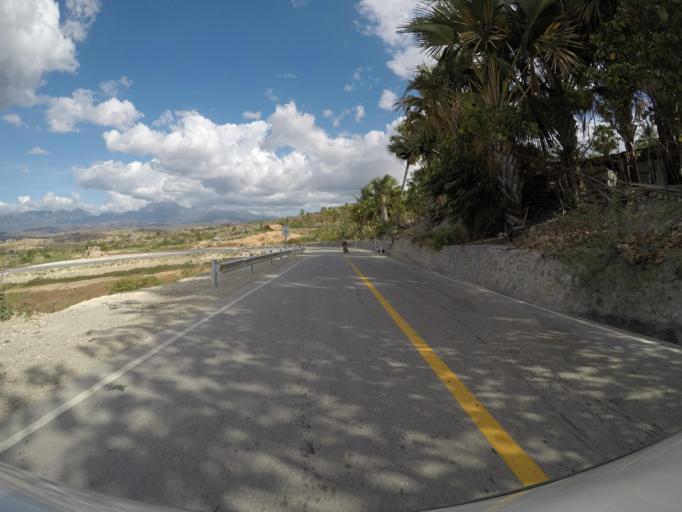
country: TL
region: Baucau
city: Baucau
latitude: -8.4725
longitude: 126.4904
